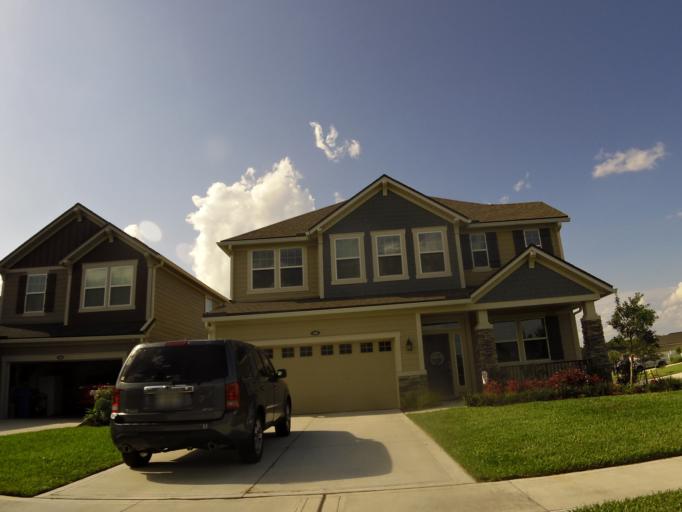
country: US
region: Florida
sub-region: Clay County
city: Green Cove Springs
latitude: 30.0241
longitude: -81.6409
